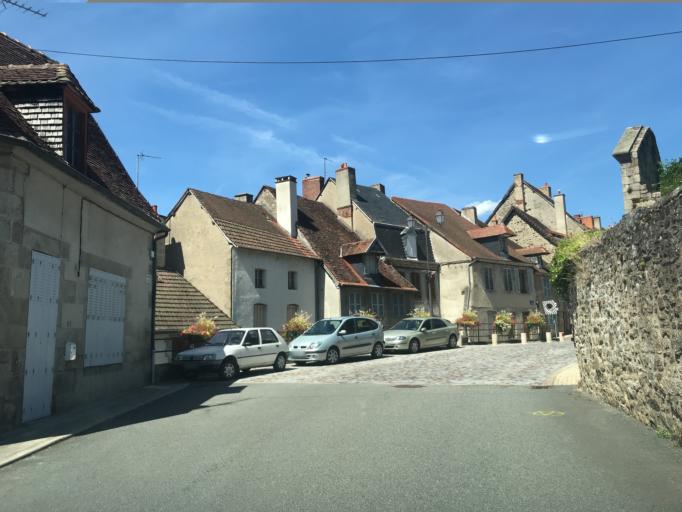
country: FR
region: Limousin
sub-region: Departement de la Creuse
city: Felletin
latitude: 45.8805
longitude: 2.1736
